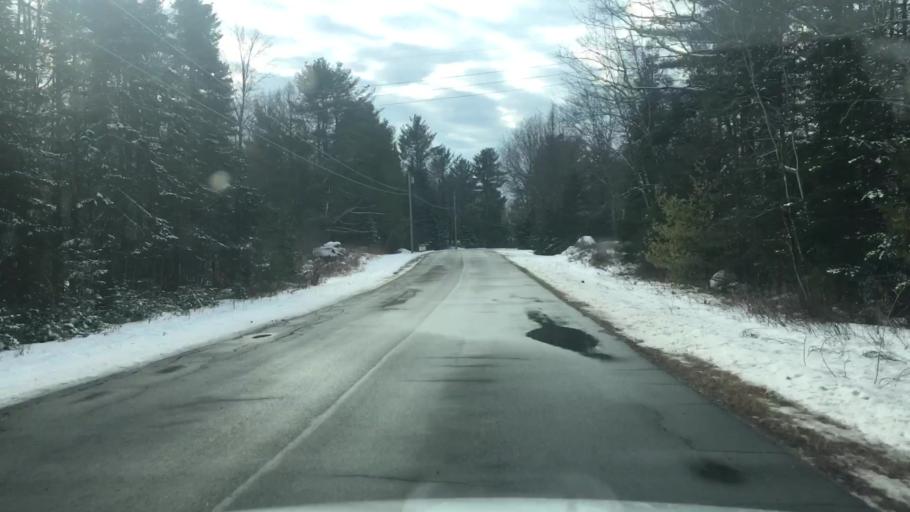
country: US
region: Maine
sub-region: Kennebec County
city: Chelsea
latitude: 44.2813
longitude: -69.6694
